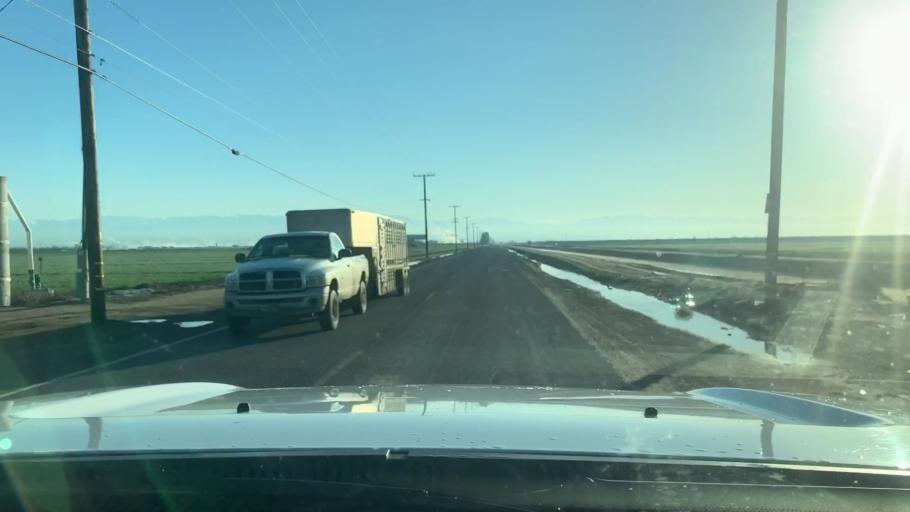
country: US
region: California
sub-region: Tulare County
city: Tulare
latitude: 36.1816
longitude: -119.3931
